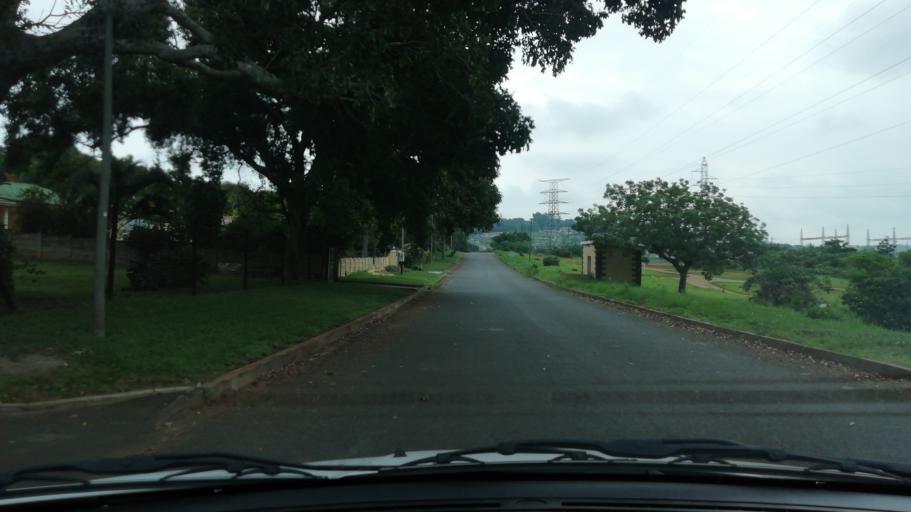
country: ZA
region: KwaZulu-Natal
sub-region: uThungulu District Municipality
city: Empangeni
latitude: -28.7374
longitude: 31.8889
